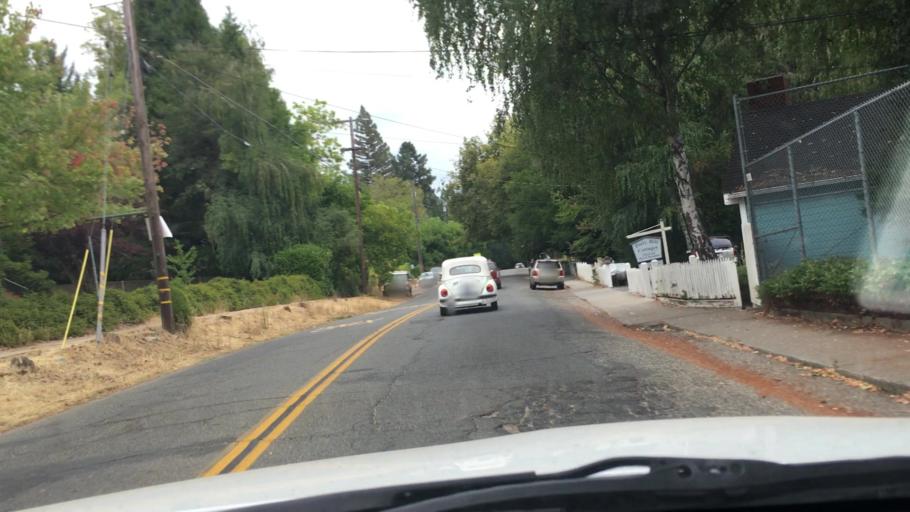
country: US
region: California
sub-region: Nevada County
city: Nevada City
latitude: 39.2570
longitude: -121.0237
